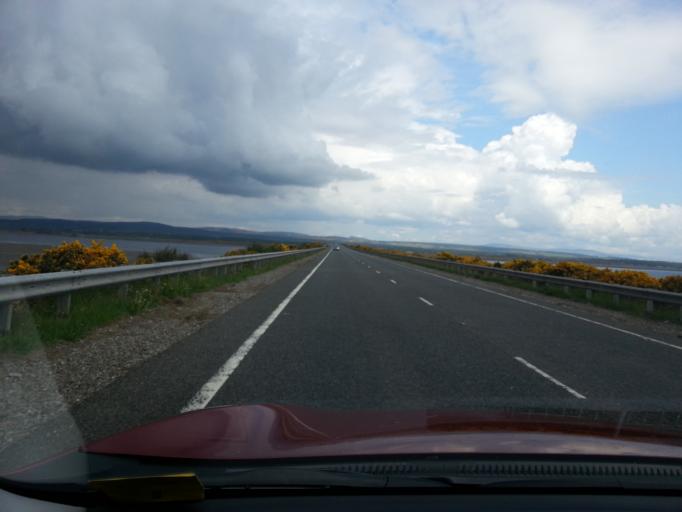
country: GB
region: Scotland
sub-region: Highland
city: Tain
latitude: 57.8369
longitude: -4.1097
